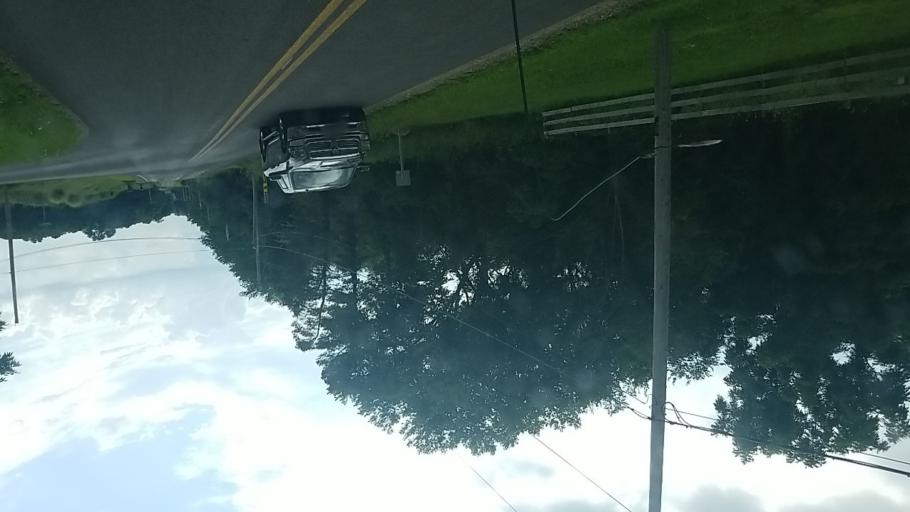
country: US
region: Ohio
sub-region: Wayne County
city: Creston
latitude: 41.0016
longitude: -81.8886
